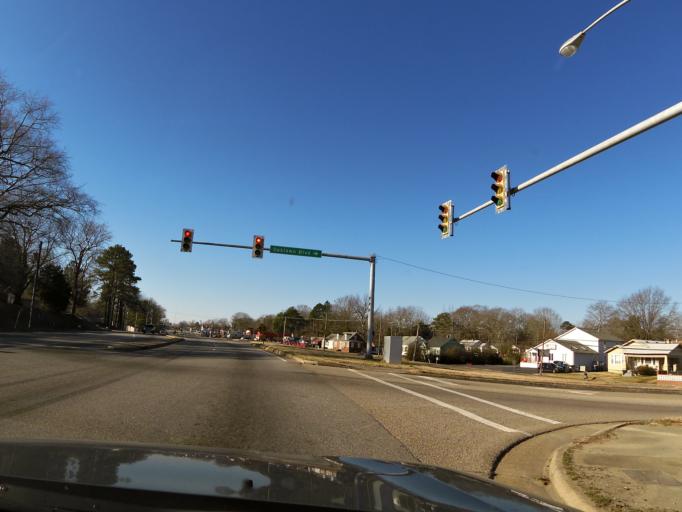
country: US
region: Virginia
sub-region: City of Hopewell
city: Hopewell
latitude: 37.2833
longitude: -77.3023
